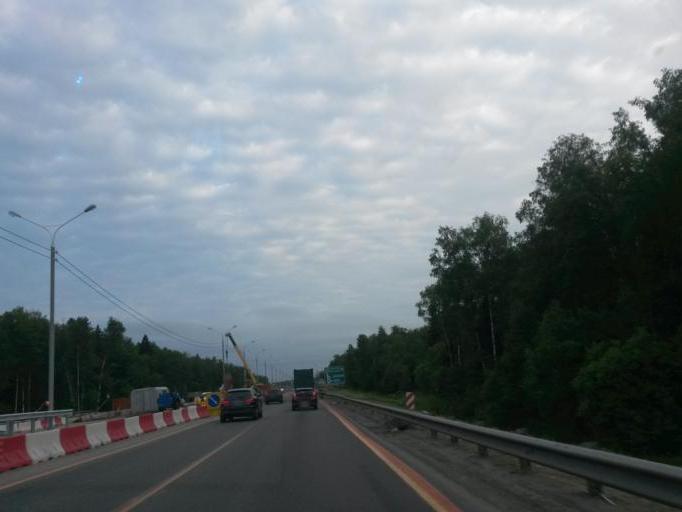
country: RU
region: Moskovskaya
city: Lyubuchany
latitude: 55.1977
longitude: 37.5346
